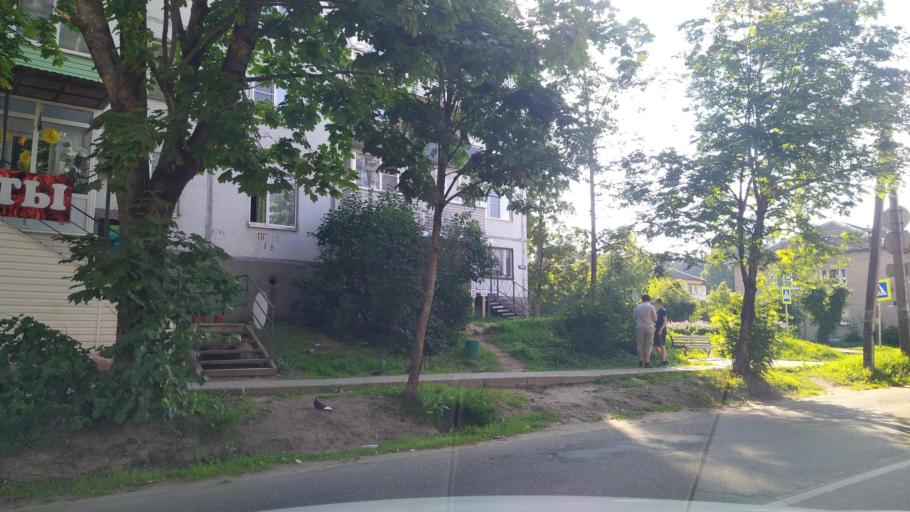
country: RU
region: Pskov
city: Pushkinskiye Gory
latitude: 57.0277
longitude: 28.9308
